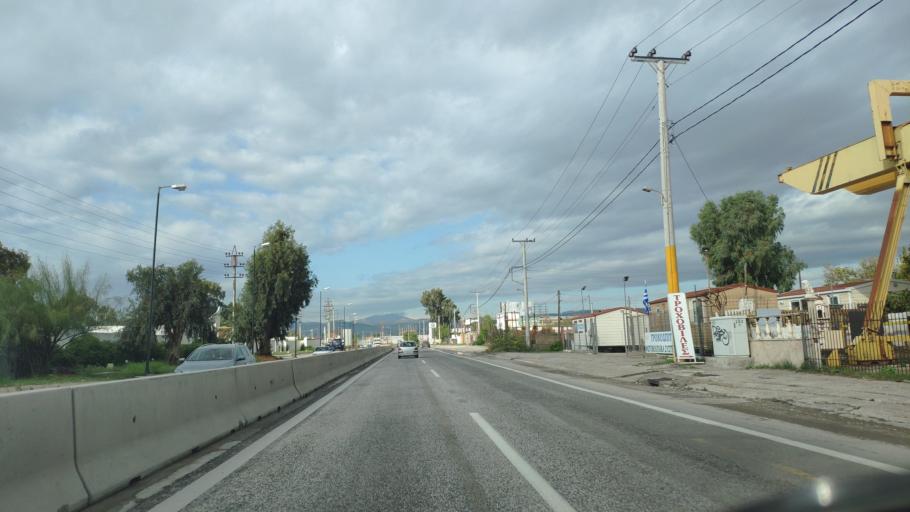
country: GR
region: Attica
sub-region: Nomarchia Dytikis Attikis
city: Aspropyrgos
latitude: 38.0467
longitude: 23.5770
